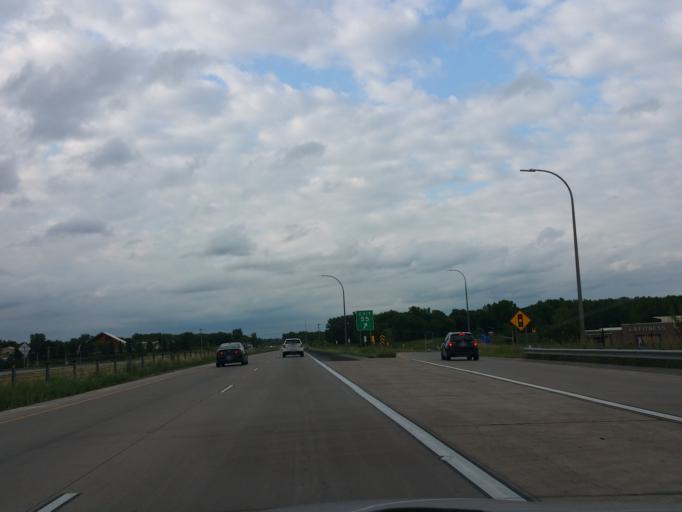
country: US
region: Minnesota
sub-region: Washington County
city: Oakdale
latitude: 44.9943
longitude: -92.9598
